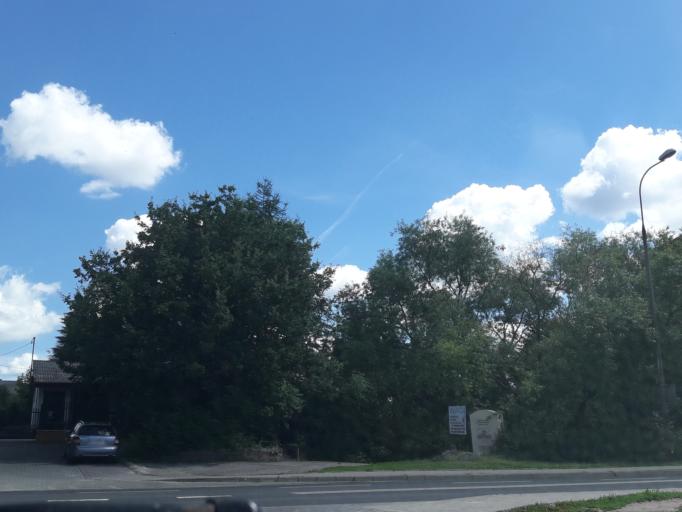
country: PL
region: Lublin Voivodeship
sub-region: Powiat lubelski
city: Lublin
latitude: 51.2535
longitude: 22.5214
